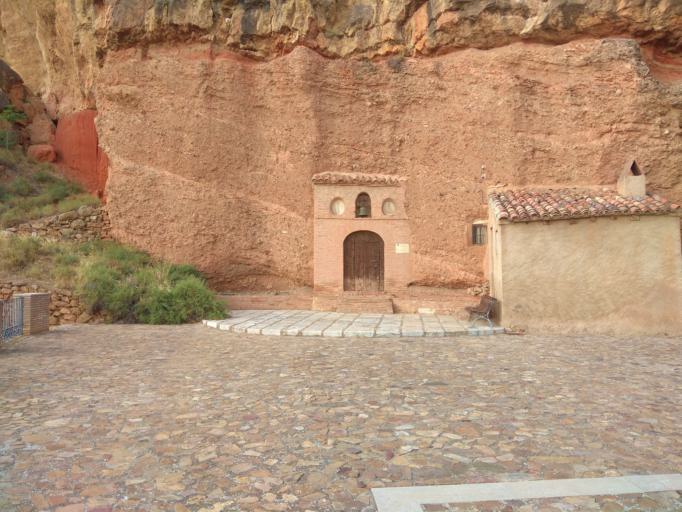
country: ES
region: Aragon
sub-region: Provincia de Zaragoza
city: Daroca
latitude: 41.1175
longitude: -1.4134
